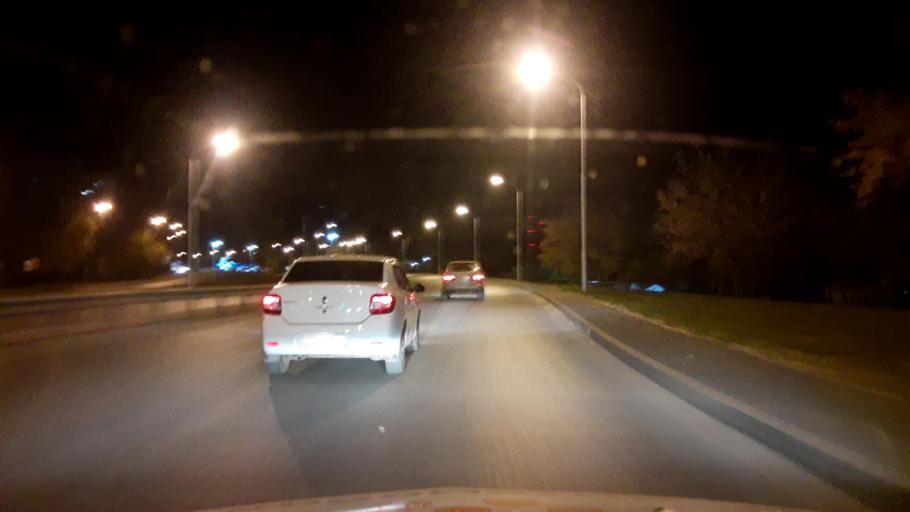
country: RU
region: Bashkortostan
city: Ufa
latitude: 54.8034
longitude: 56.1119
